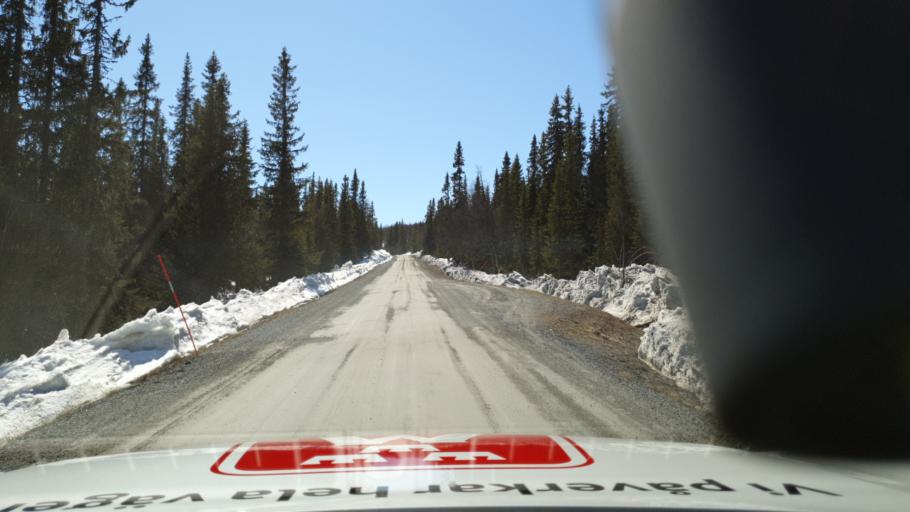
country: SE
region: Jaemtland
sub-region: Are Kommun
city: Are
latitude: 62.7983
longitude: 12.7642
